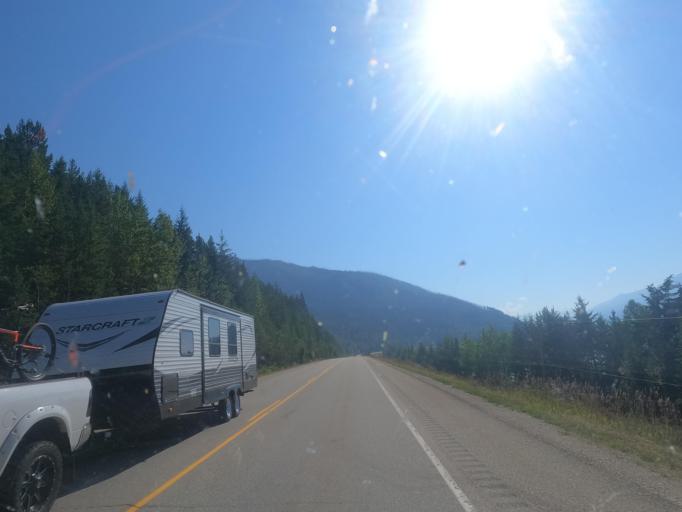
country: CA
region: Alberta
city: Jasper Park Lodge
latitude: 52.9540
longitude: -118.8801
